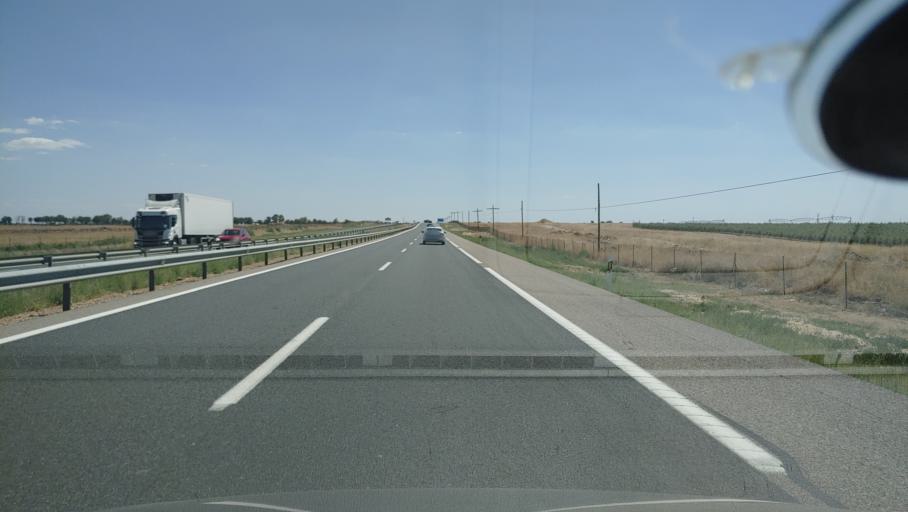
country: ES
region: Castille-La Mancha
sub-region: Provincia de Ciudad Real
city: Villarta de San Juan
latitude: 39.1388
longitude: -3.3827
